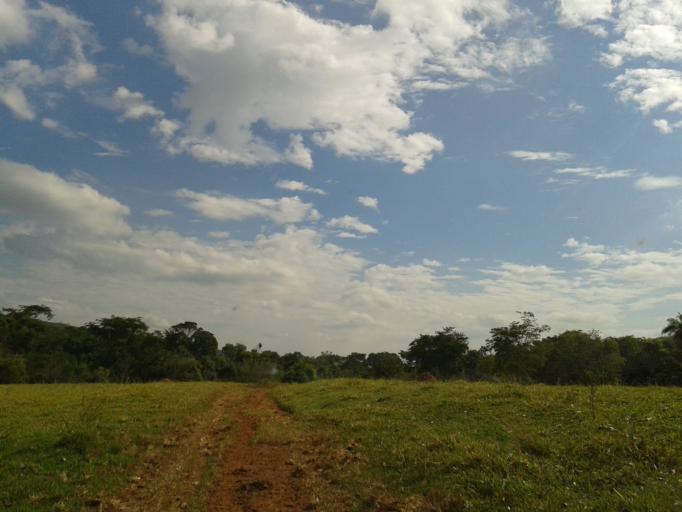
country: BR
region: Minas Gerais
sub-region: Campina Verde
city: Campina Verde
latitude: -19.3949
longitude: -49.6672
